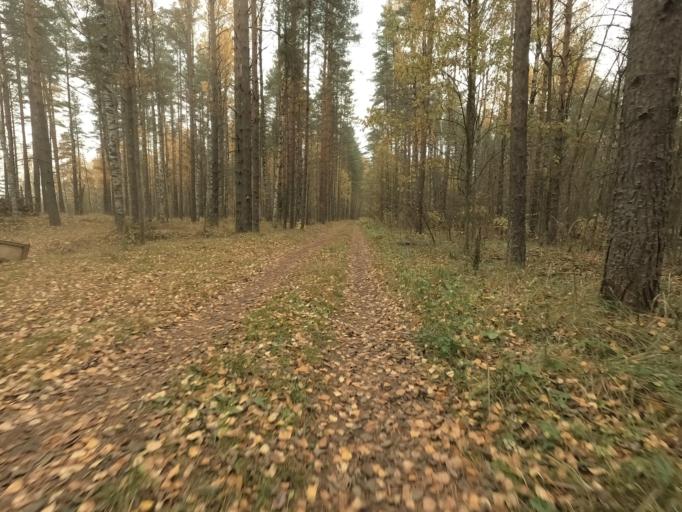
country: RU
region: Leningrad
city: Kirovsk
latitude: 59.8555
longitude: 30.9931
